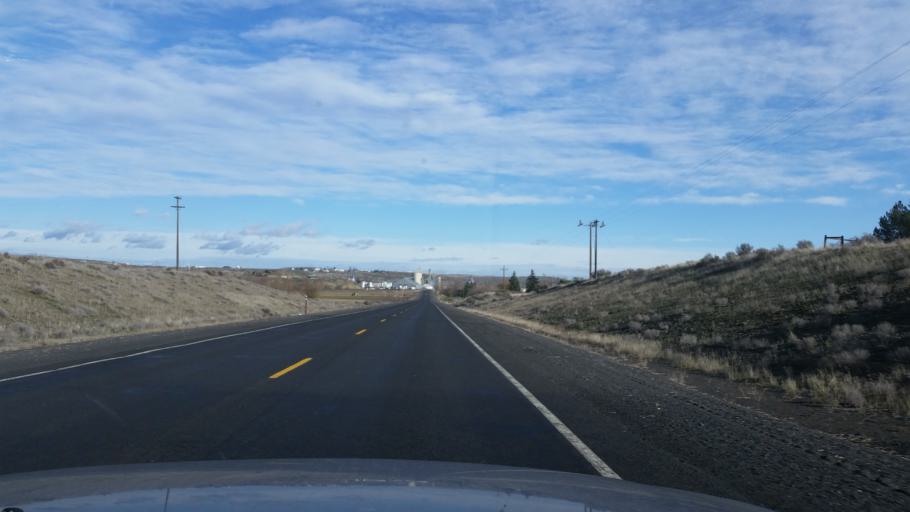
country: US
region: Washington
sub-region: Adams County
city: Ritzville
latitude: 47.3284
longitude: -118.7117
